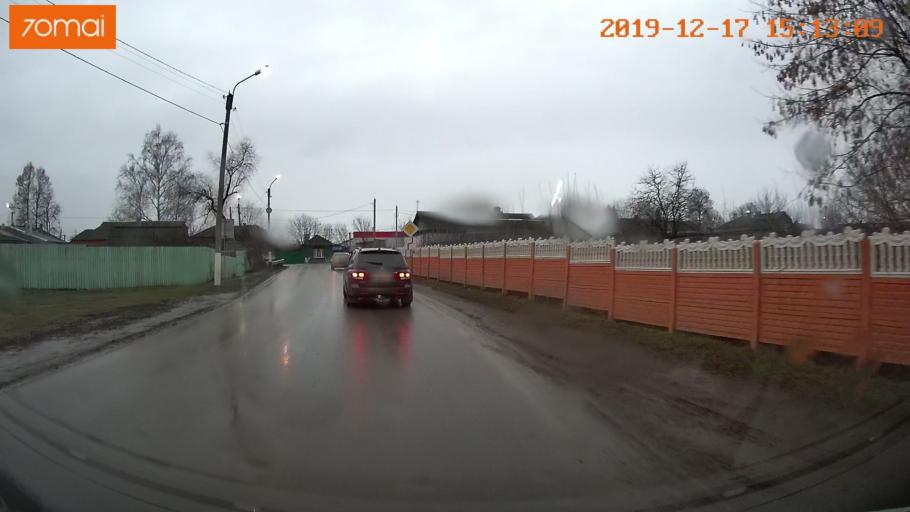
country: RU
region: Rjazan
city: Mikhaylov
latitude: 54.2347
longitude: 39.0211
